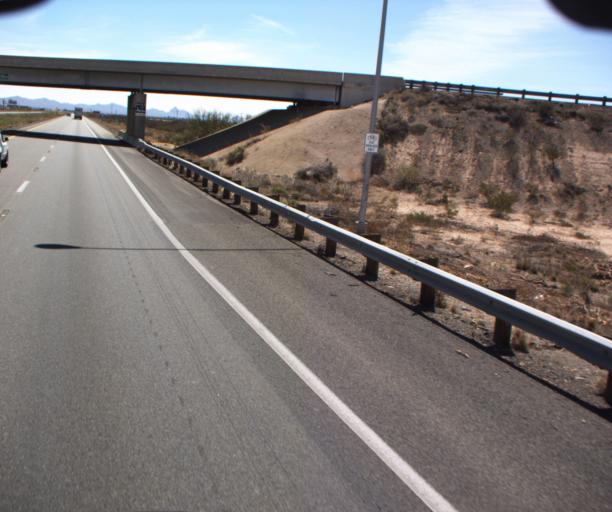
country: US
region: New Mexico
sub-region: Hidalgo County
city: Lordsburg
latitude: 32.2720
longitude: -109.2504
